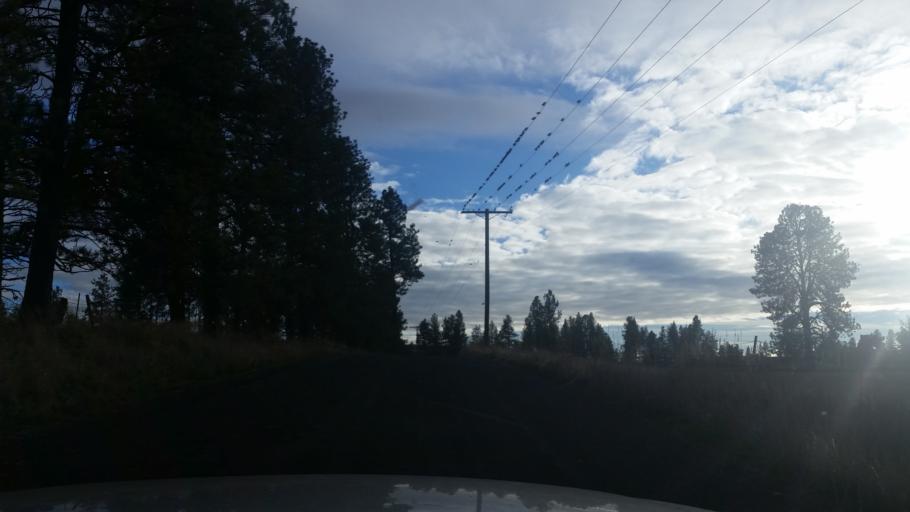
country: US
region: Washington
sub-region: Spokane County
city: Cheney
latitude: 47.4293
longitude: -117.4344
